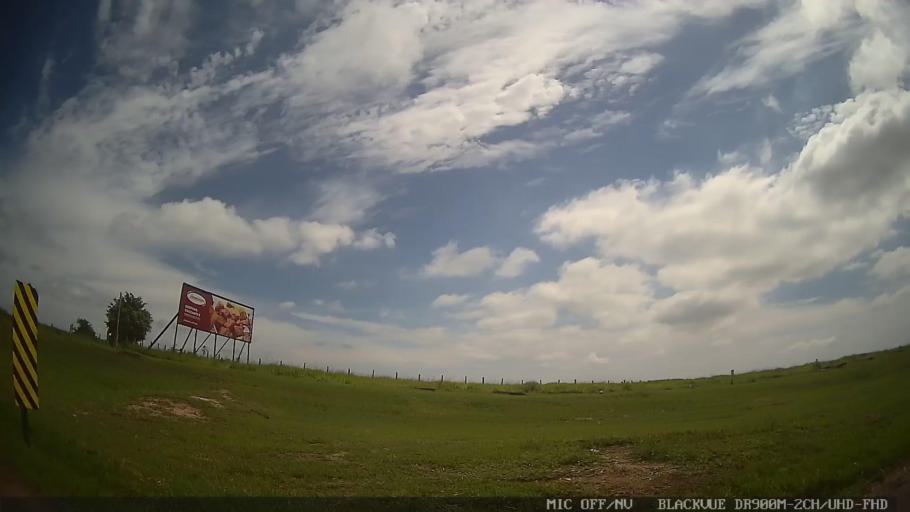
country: BR
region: Sao Paulo
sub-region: Tiete
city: Tiete
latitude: -23.1002
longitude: -47.7727
